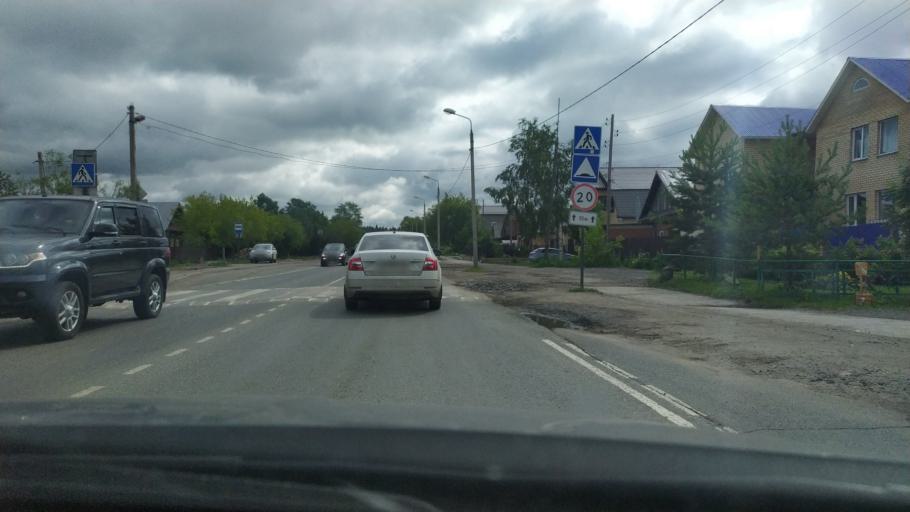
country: RU
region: Perm
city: Froly
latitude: 57.9770
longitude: 56.3069
